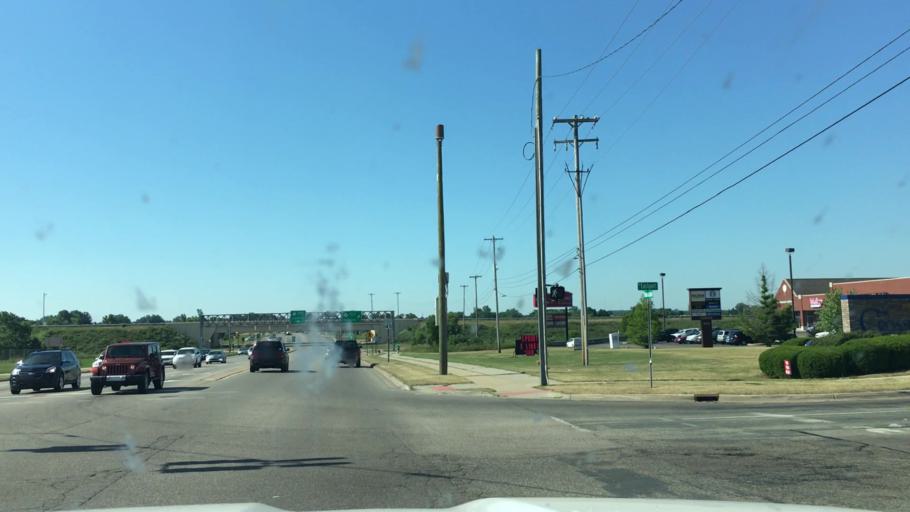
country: US
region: Michigan
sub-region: Kent County
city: Kentwood
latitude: 42.8499
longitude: -85.6249
